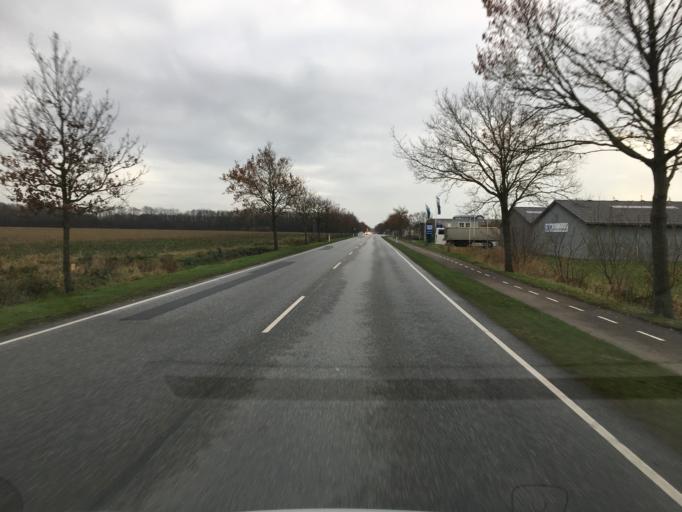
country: DK
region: South Denmark
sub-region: Tonder Kommune
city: Tonder
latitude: 54.9580
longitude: 8.8690
